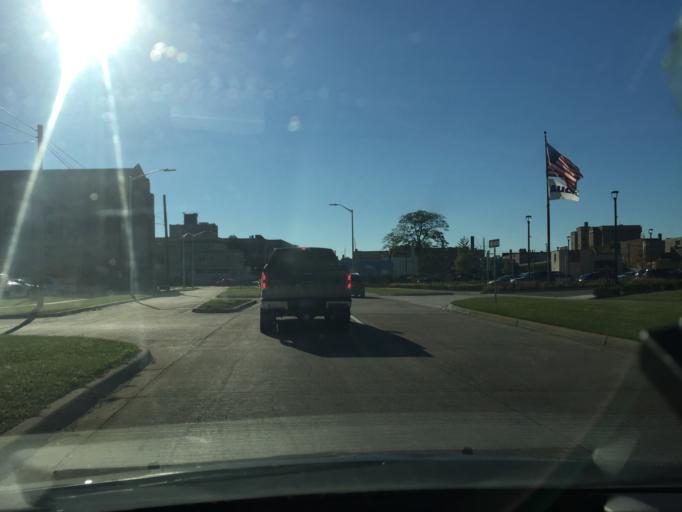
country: US
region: Michigan
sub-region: Oakland County
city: Pontiac
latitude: 42.6404
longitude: -83.2896
